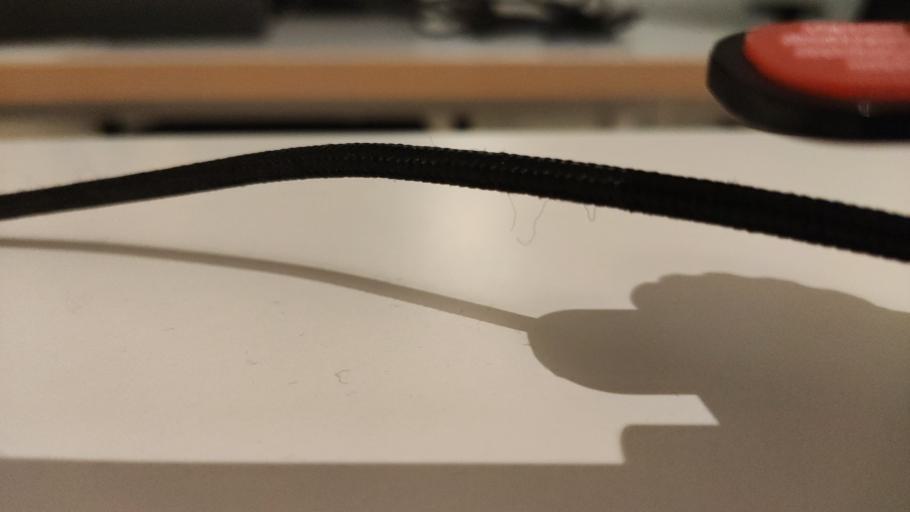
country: RU
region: Moskovskaya
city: Meshcherino
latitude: 55.1703
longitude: 38.3276
